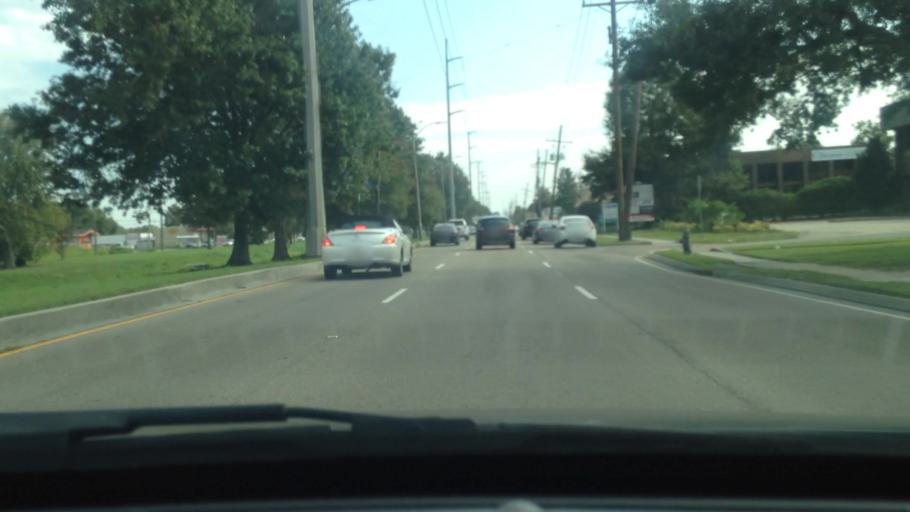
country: US
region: Louisiana
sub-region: Jefferson Parish
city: Terrytown
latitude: 29.9274
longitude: -90.0276
